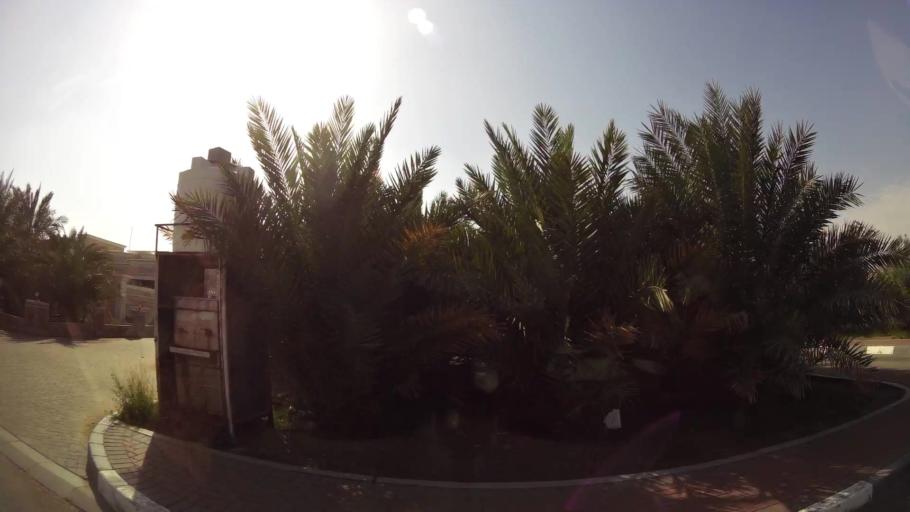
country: AE
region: Abu Dhabi
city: Al Ain
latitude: 24.0711
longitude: 55.8732
